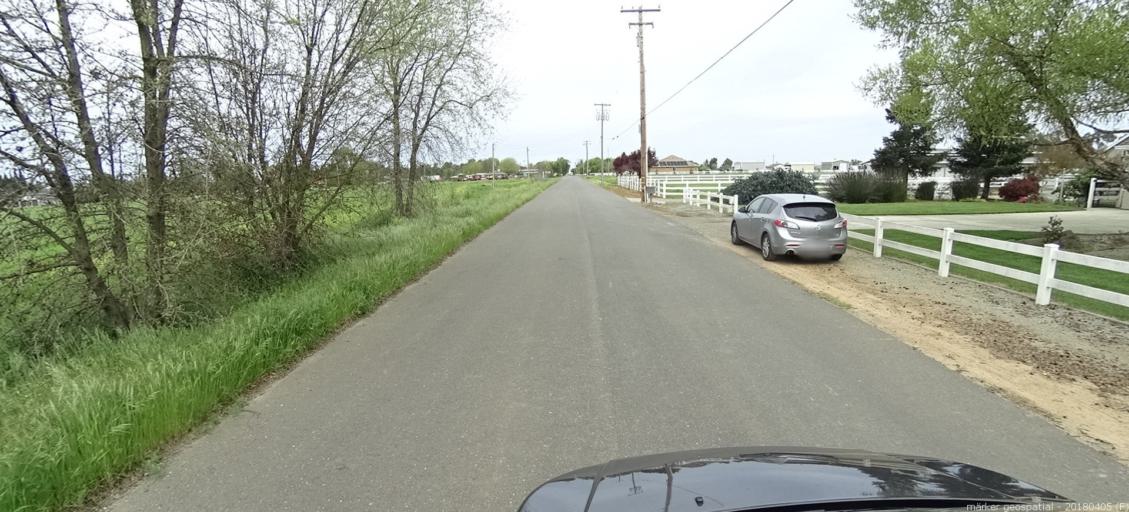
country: US
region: California
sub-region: Sacramento County
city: Galt
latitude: 38.2820
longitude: -121.3259
